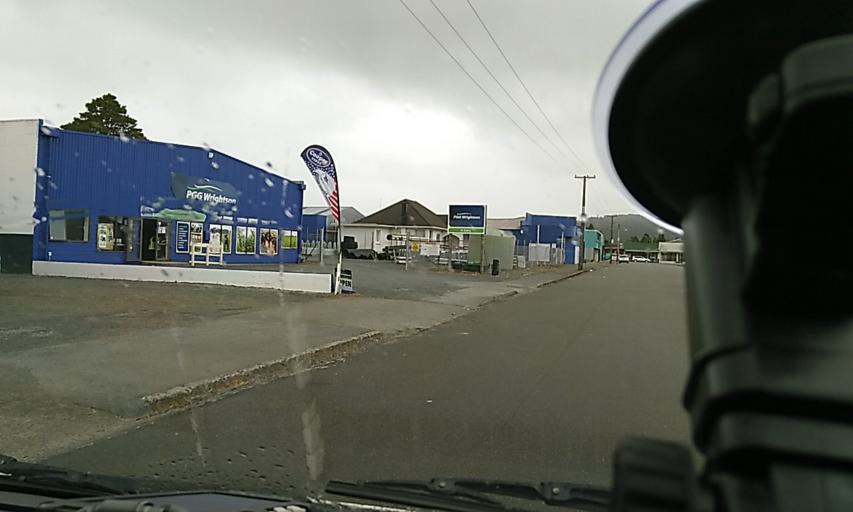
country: NZ
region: Northland
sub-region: Far North District
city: Waimate North
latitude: -35.4085
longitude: 173.8018
